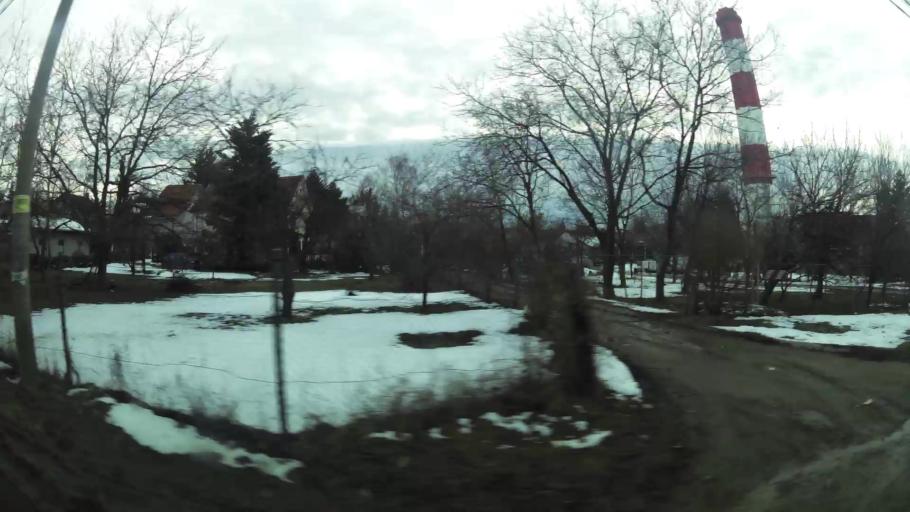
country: RS
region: Central Serbia
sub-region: Belgrade
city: Vozdovac
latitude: 44.7539
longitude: 20.4888
